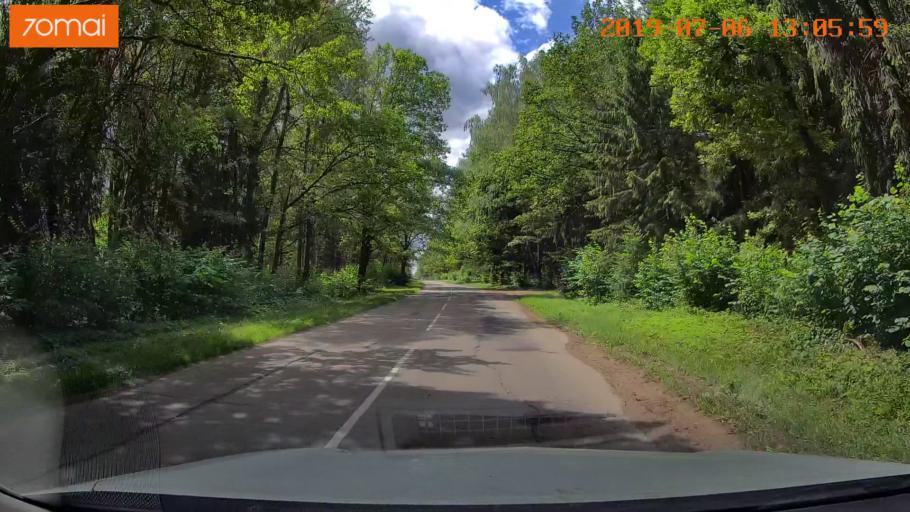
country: BY
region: Minsk
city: Dzyarzhynsk
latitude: 53.6850
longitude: 27.0592
